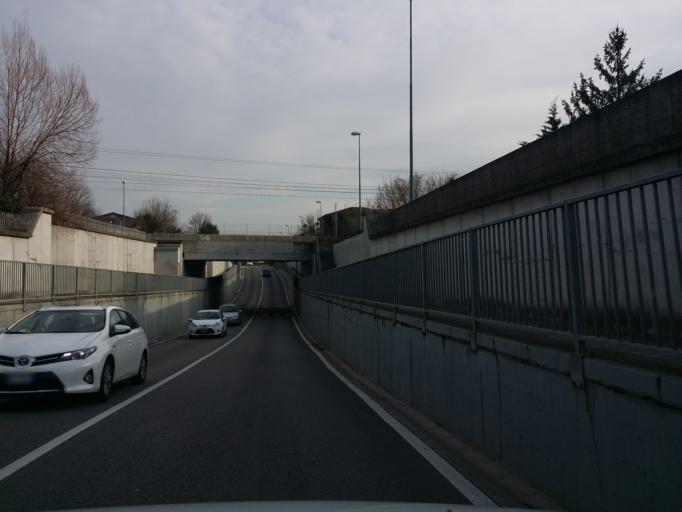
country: IT
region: Veneto
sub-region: Provincia di Padova
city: Abano Terme
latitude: 45.3543
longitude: 11.8101
